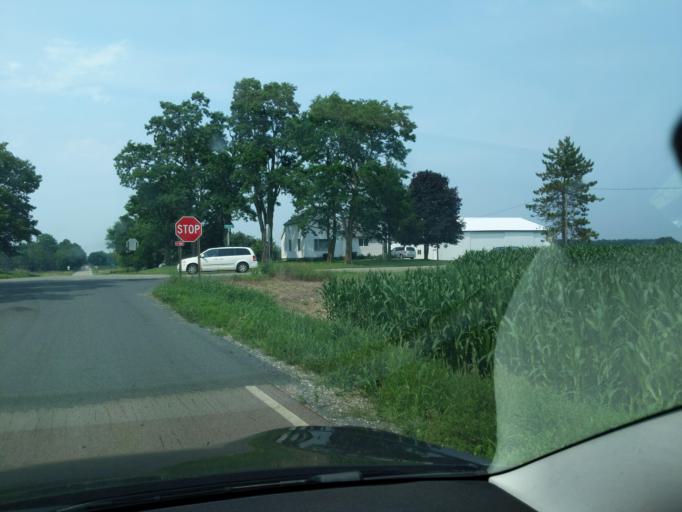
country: US
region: Michigan
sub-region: Clinton County
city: Saint Johns
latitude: 42.9288
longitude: -84.5822
